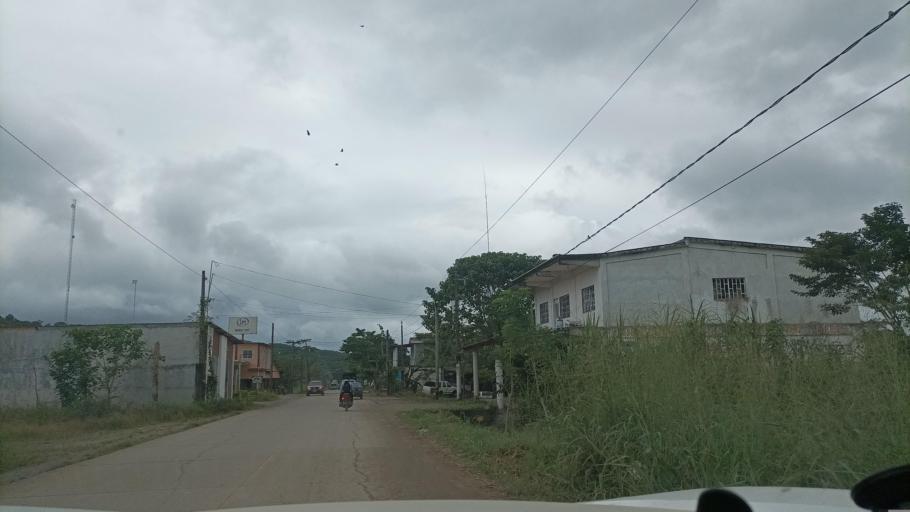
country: MX
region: Veracruz
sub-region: Uxpanapa
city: Poblado 10
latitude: 17.2790
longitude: -94.4559
